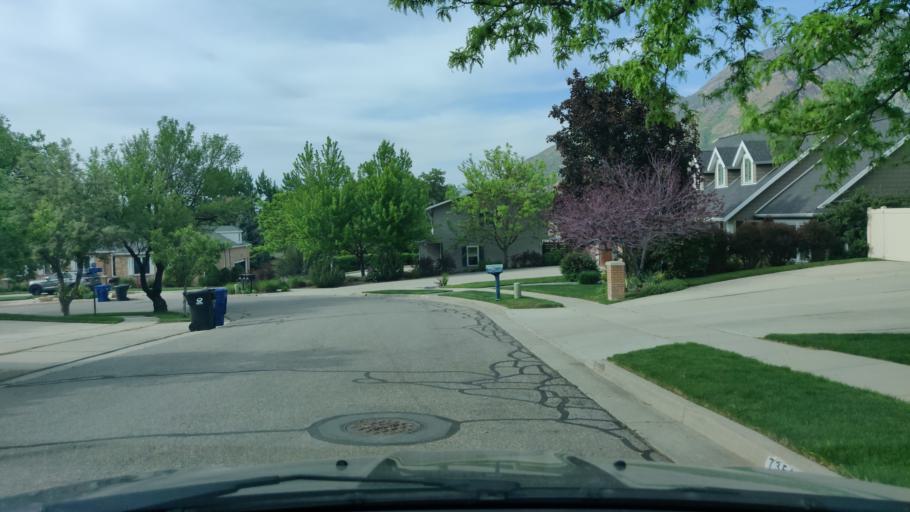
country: US
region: Utah
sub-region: Salt Lake County
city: Cottonwood Heights
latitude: 40.6174
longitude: -111.8063
